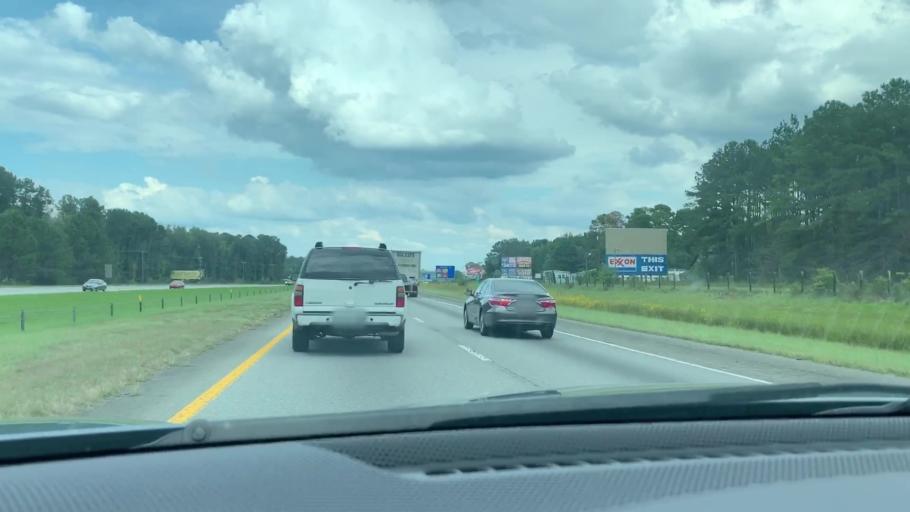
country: US
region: South Carolina
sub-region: Hampton County
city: Yemassee
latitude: 32.6180
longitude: -80.8912
